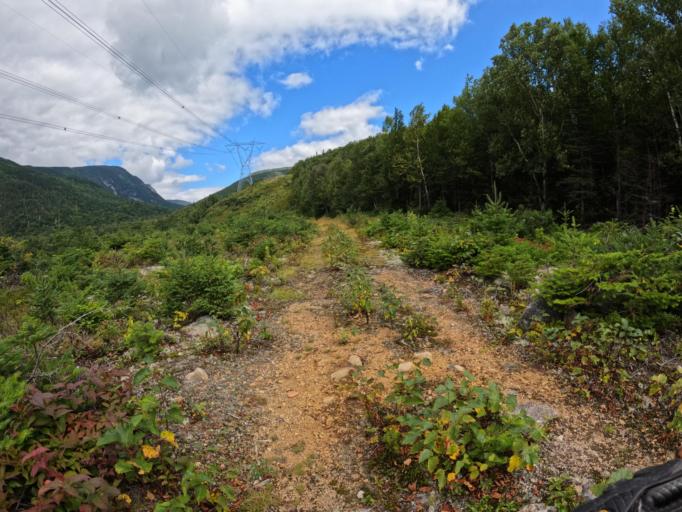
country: CA
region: Quebec
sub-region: Capitale-Nationale
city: La Malbaie
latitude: 47.8852
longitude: -70.3840
